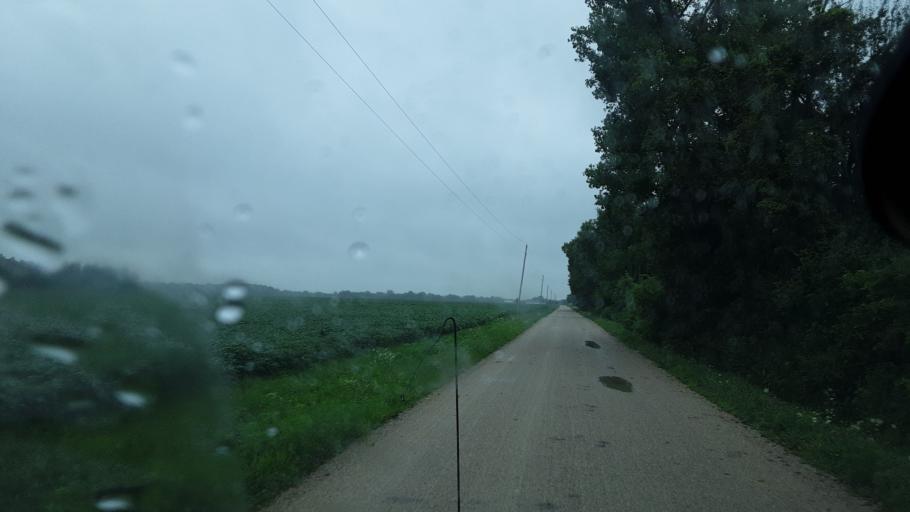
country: US
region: Indiana
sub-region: Adams County
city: Berne
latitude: 40.7038
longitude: -84.8134
